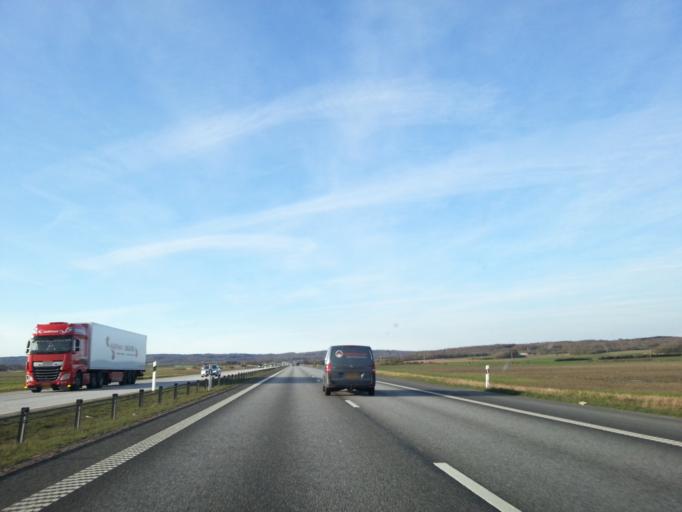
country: SE
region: Skane
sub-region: Angelholms Kommun
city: AEngelholm
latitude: 56.2853
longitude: 12.9000
